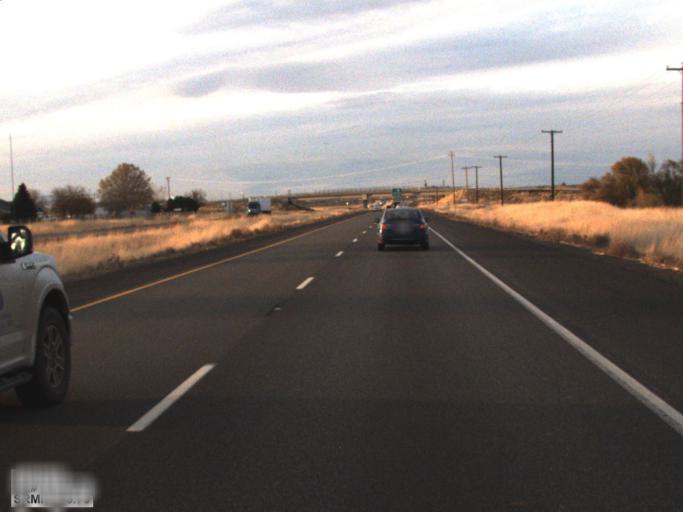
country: US
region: Washington
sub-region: Walla Walla County
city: Burbank
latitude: 46.1949
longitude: -118.9921
